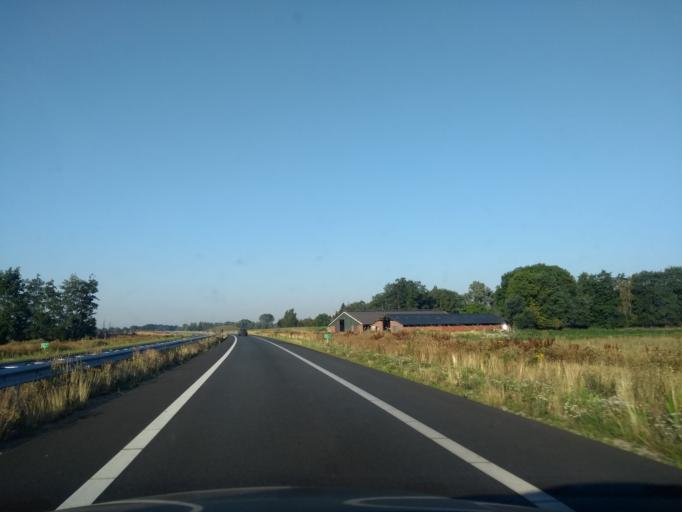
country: NL
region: Gelderland
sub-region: Berkelland
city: Neede
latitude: 52.1158
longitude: 6.6291
